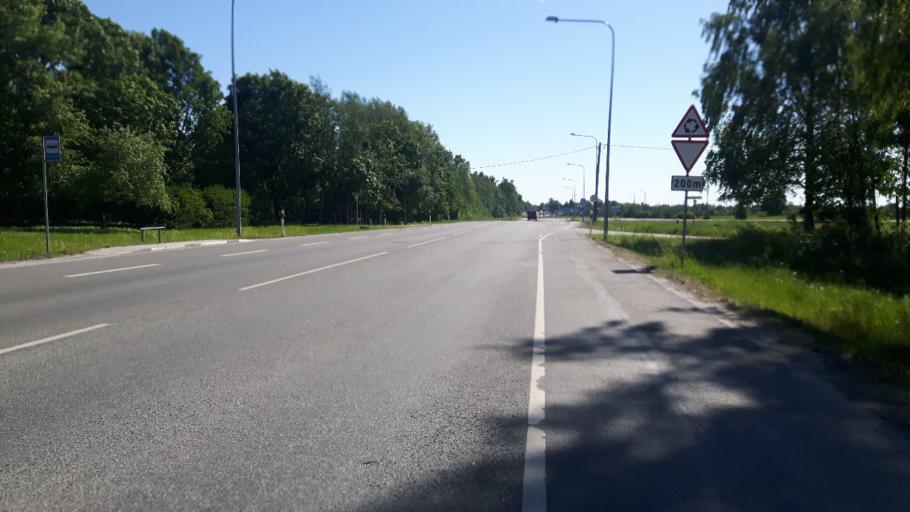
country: EE
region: Raplamaa
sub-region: Rapla vald
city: Rapla
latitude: 59.0165
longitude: 24.8038
